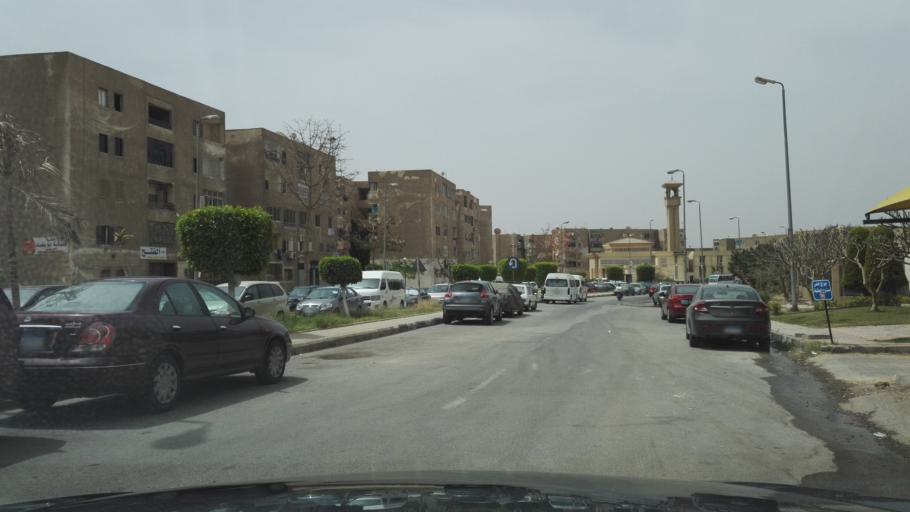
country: EG
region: Muhafazat al Qahirah
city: Cairo
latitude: 29.9957
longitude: 31.4243
